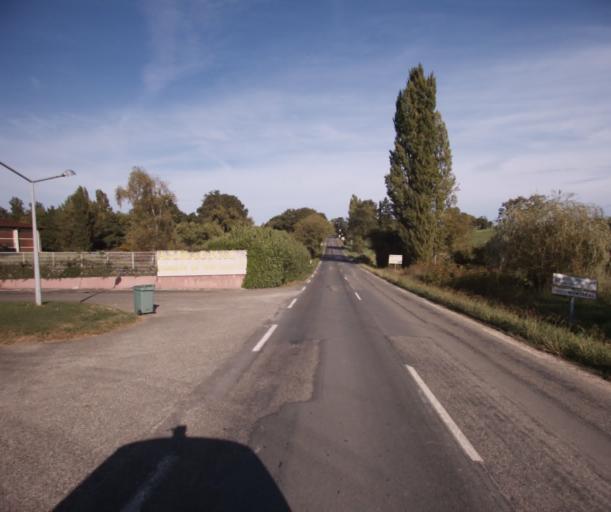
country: FR
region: Midi-Pyrenees
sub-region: Departement du Gers
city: Eauze
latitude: 43.8582
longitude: 0.0836
